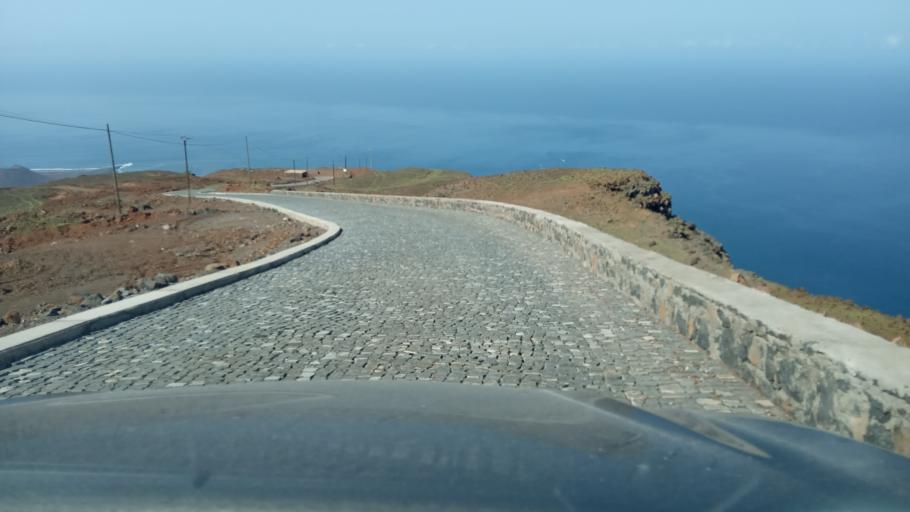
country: CV
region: Porto Novo
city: Porto Novo
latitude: 16.9589
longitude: -25.2983
